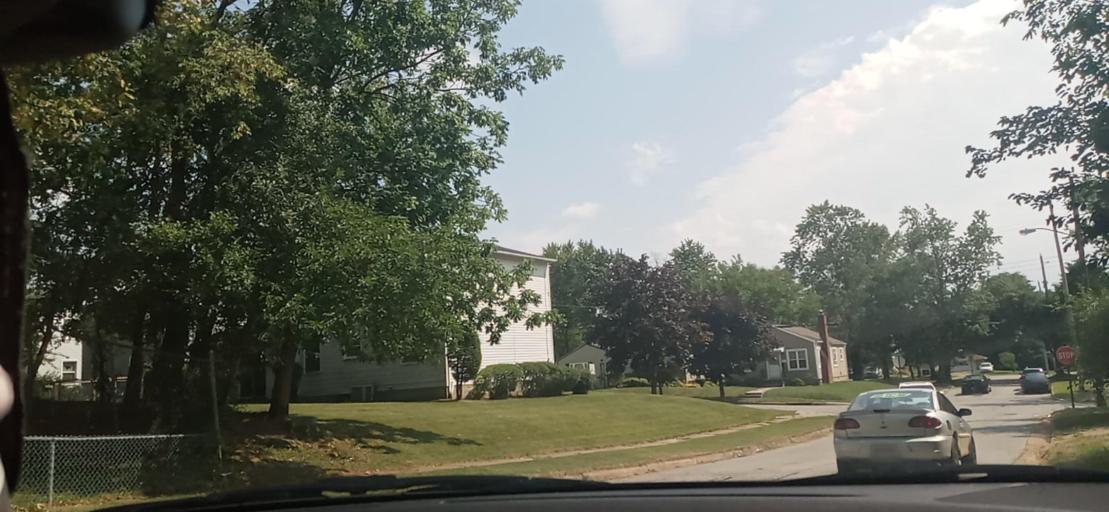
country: US
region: Ohio
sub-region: Summit County
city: Akron
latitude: 41.0620
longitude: -81.5610
